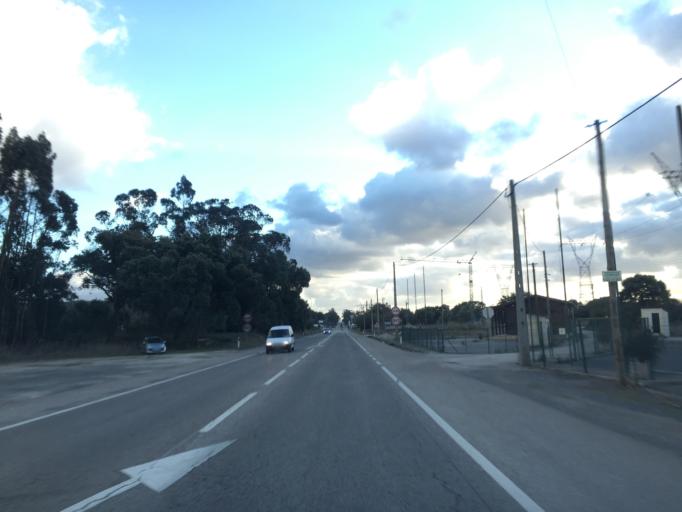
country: PT
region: Leiria
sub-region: Alcobaca
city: Turquel
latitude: 39.4680
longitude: -8.9422
